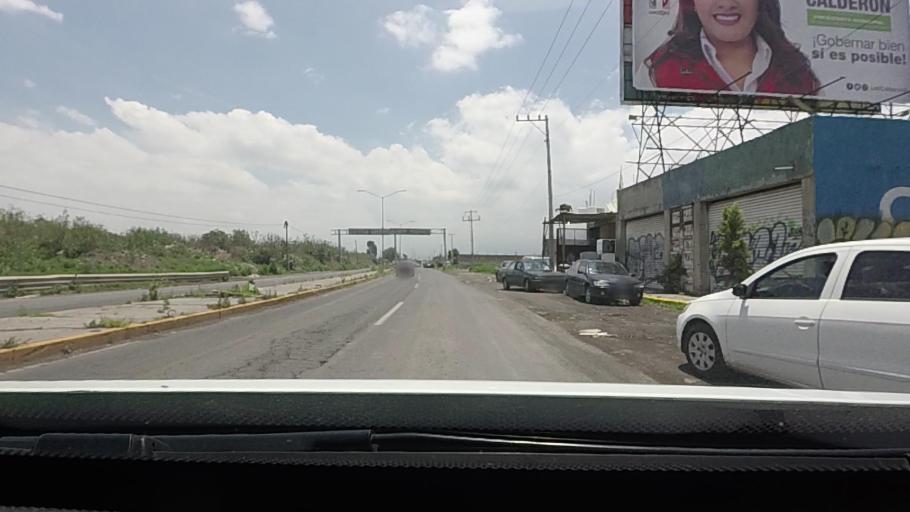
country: MX
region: Mexico
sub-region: Chalco
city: Barrio de Guadalupe
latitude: 19.2483
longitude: -98.9211
